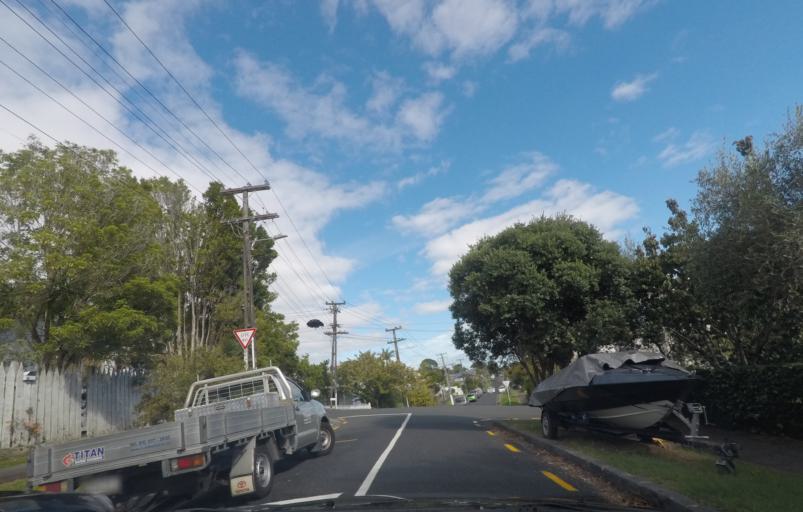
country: NZ
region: Auckland
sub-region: Auckland
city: Auckland
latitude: -36.8697
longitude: 174.7415
